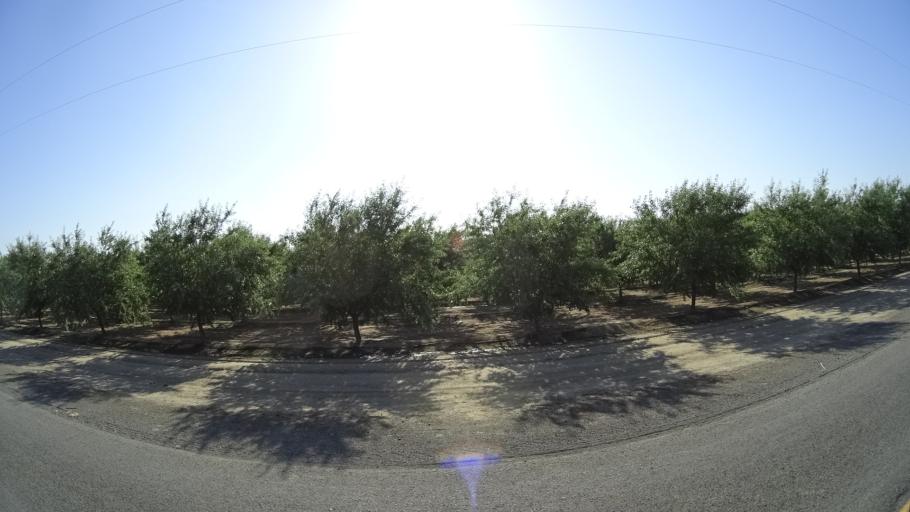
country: US
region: California
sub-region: Kings County
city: Home Garden
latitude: 36.2726
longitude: -119.5652
